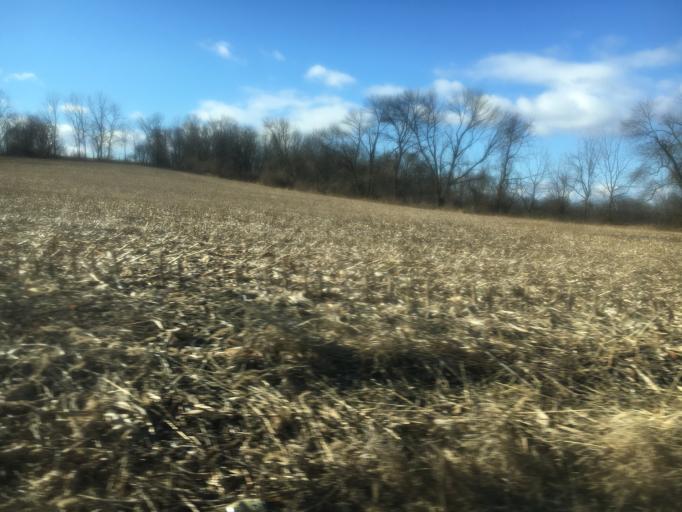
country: US
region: Pennsylvania
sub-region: Lehigh County
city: Egypt
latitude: 40.6520
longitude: -75.5516
